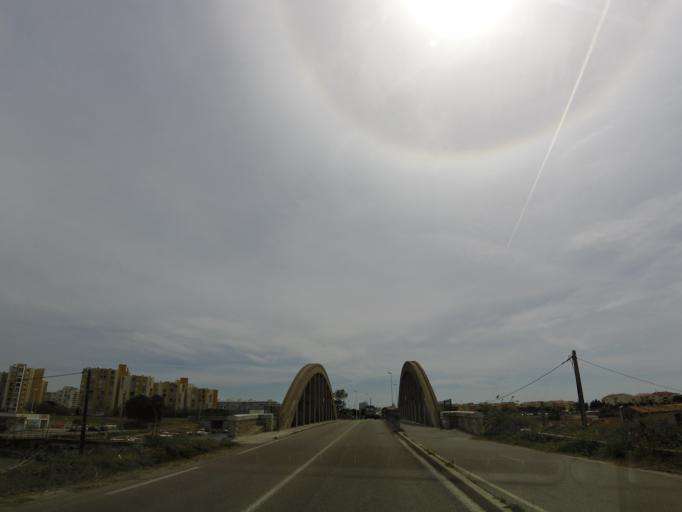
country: FR
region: Languedoc-Roussillon
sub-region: Departement de l'Herault
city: Perols
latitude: 43.5477
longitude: 3.9698
